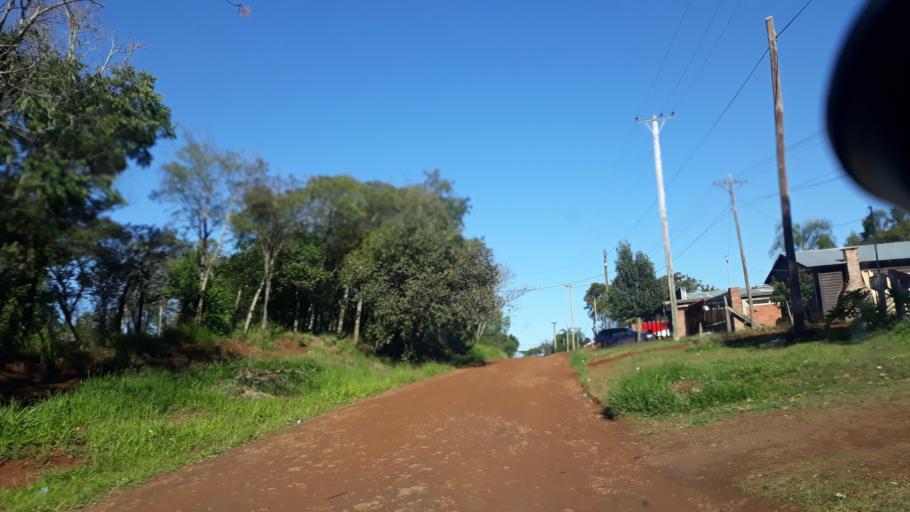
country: AR
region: Misiones
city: Bernardo de Irigoyen
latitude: -26.2640
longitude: -53.6583
